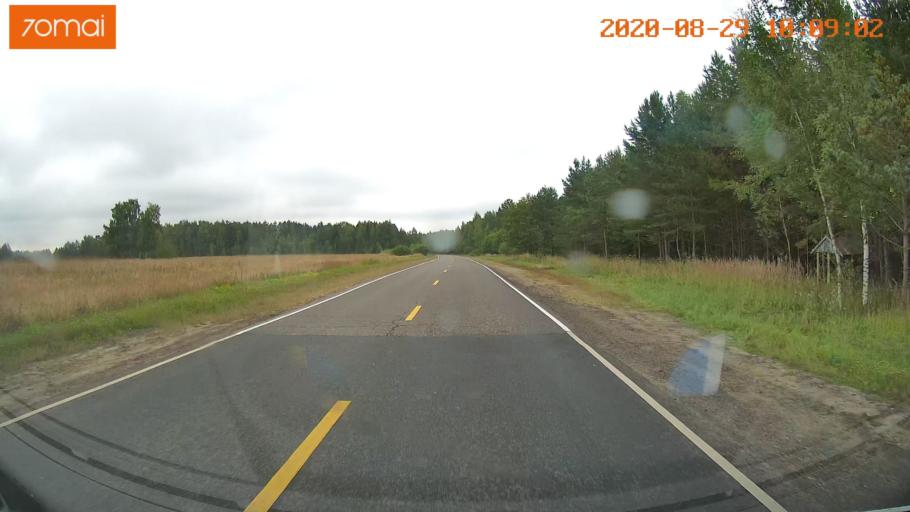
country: RU
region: Ivanovo
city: Kuznechikha
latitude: 57.3743
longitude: 42.6058
